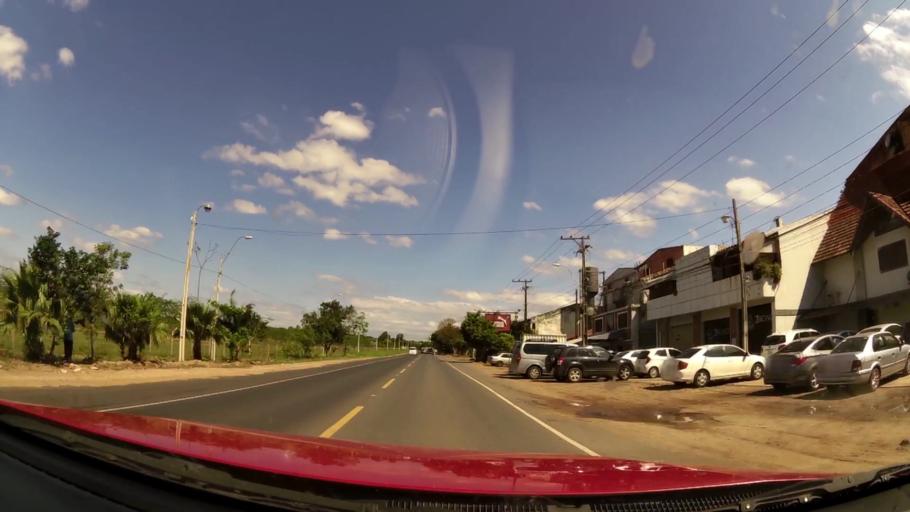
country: PY
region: Central
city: Fernando de la Mora
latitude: -25.2768
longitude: -57.5397
